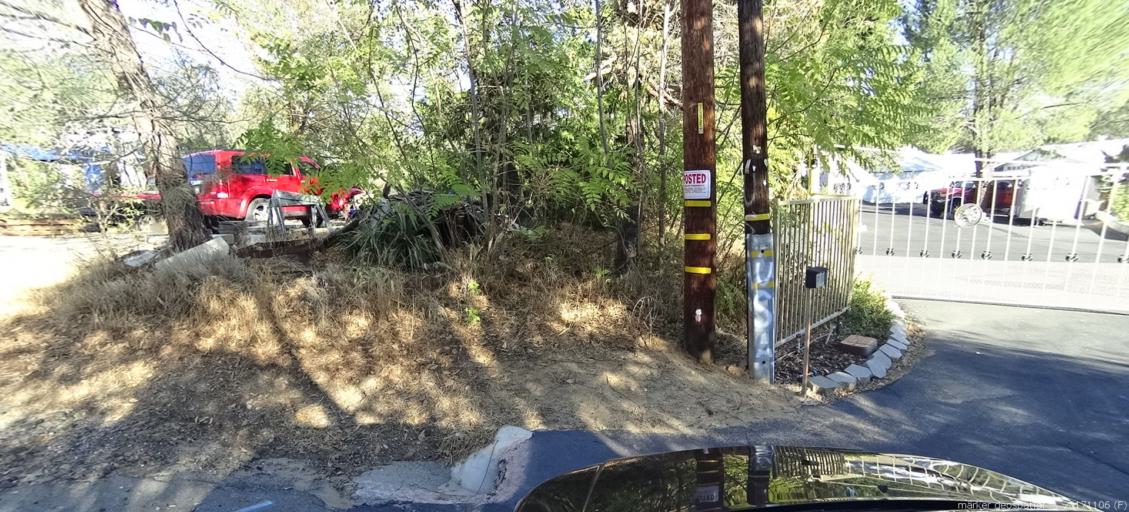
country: US
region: California
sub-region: Shasta County
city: Shasta
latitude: 40.5934
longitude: -122.4874
